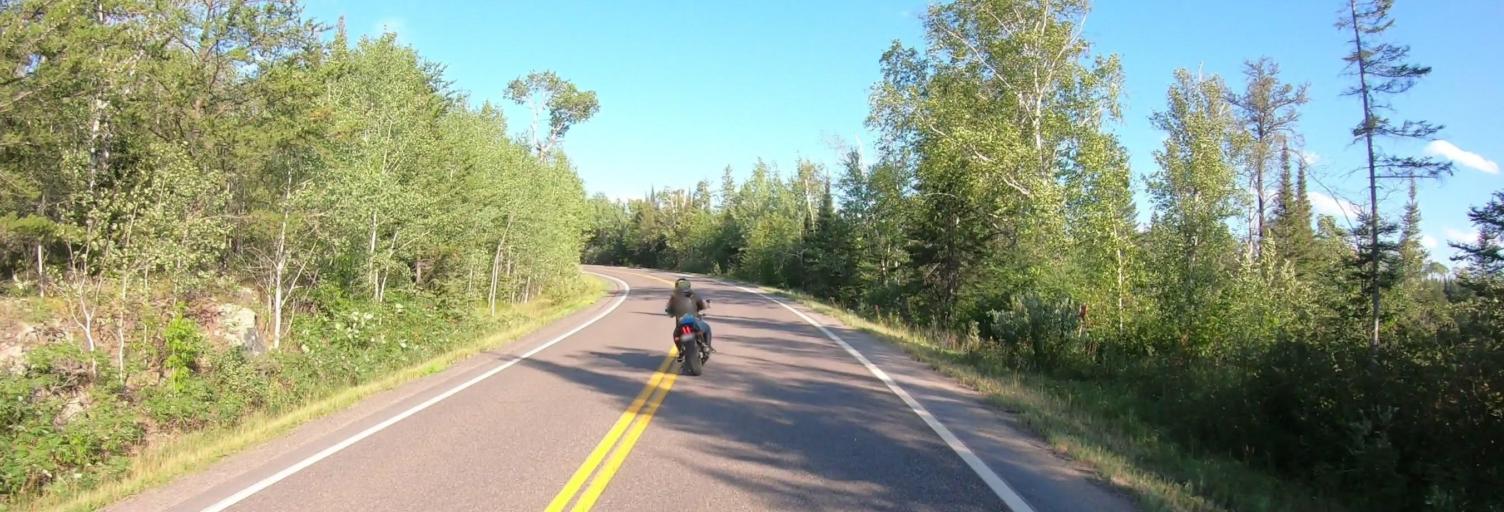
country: US
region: Minnesota
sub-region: Saint Louis County
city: Ely
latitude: 47.9593
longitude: -91.5551
